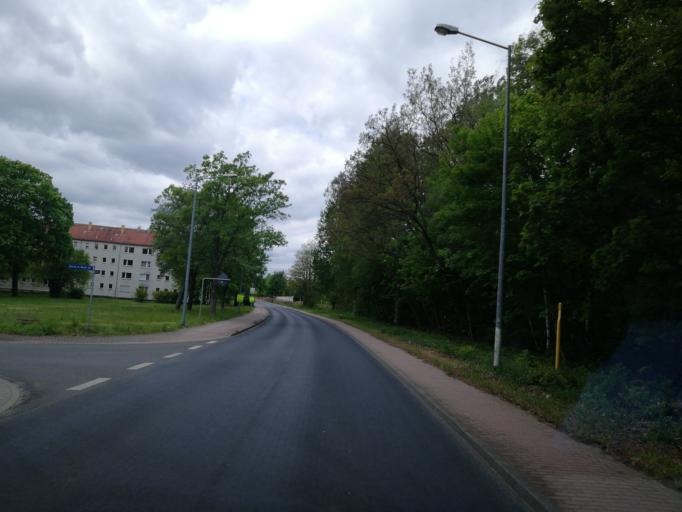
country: DE
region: Brandenburg
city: Lauchhammer
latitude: 51.5013
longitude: 13.7695
